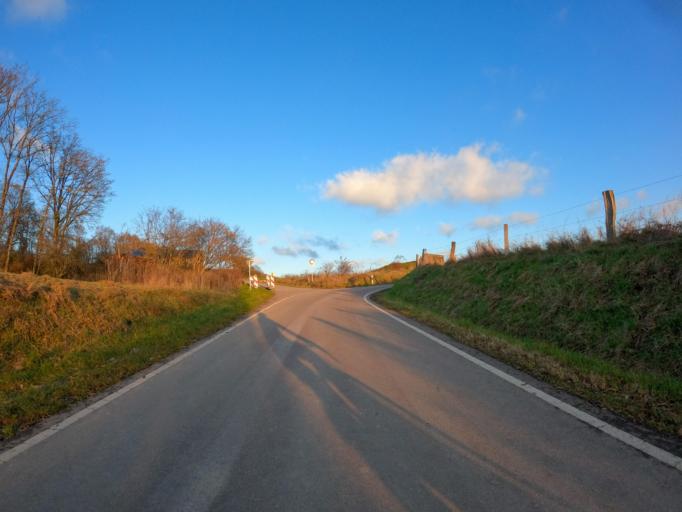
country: LU
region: Diekirch
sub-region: Canton de Wiltz
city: Bavigne
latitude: 49.9249
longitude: 5.8532
